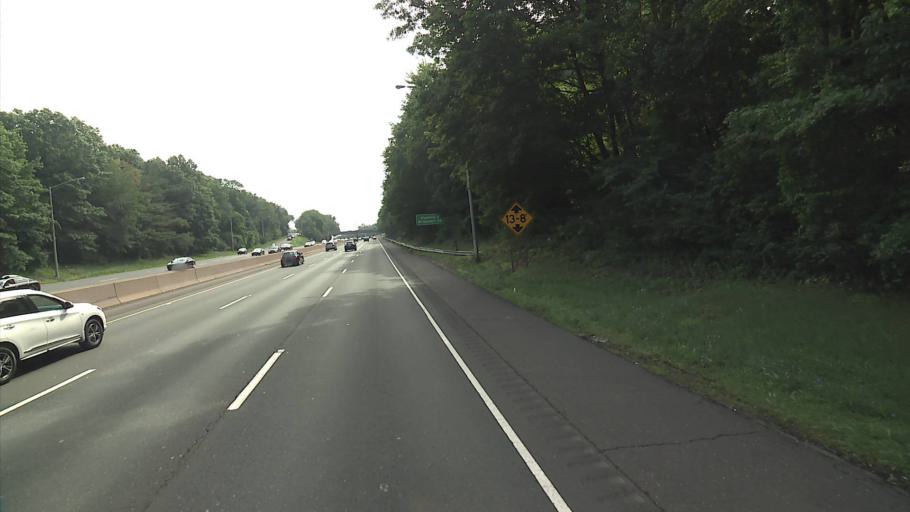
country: US
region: Connecticut
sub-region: Fairfield County
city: Riverside
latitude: 41.0400
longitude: -73.5824
